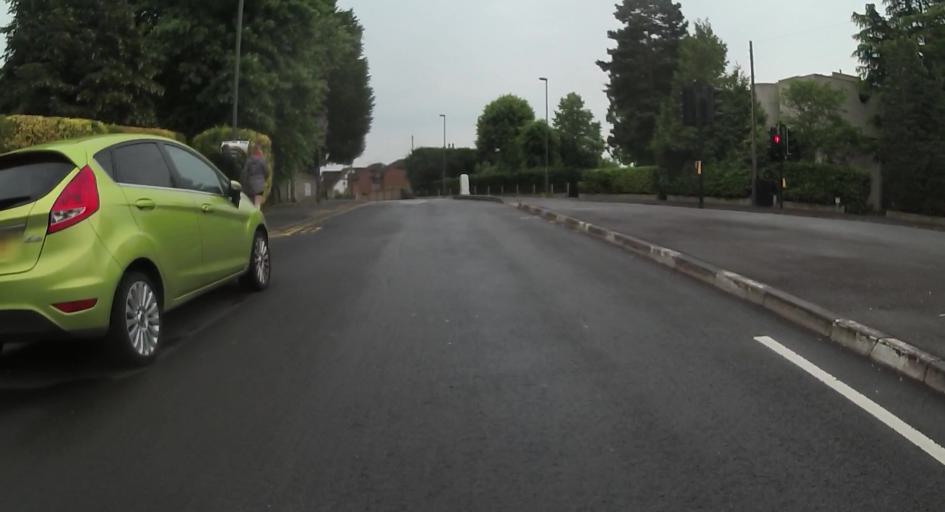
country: GB
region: England
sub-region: Surrey
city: Frimley
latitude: 51.3153
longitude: -0.7398
